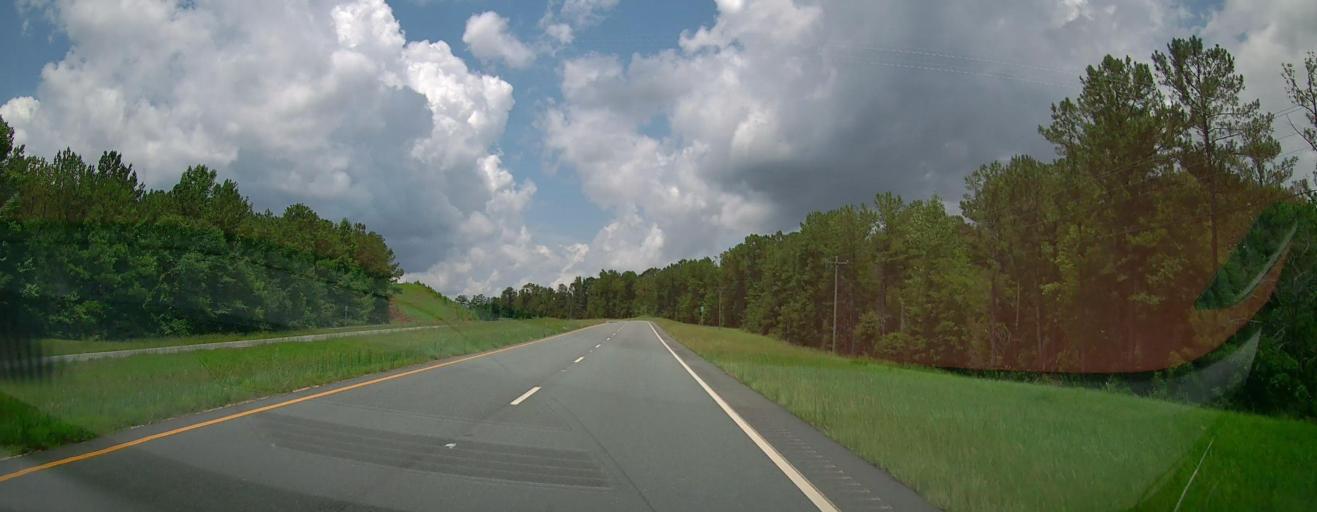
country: US
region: Georgia
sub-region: Upson County
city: Thomaston
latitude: 32.8137
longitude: -84.2865
